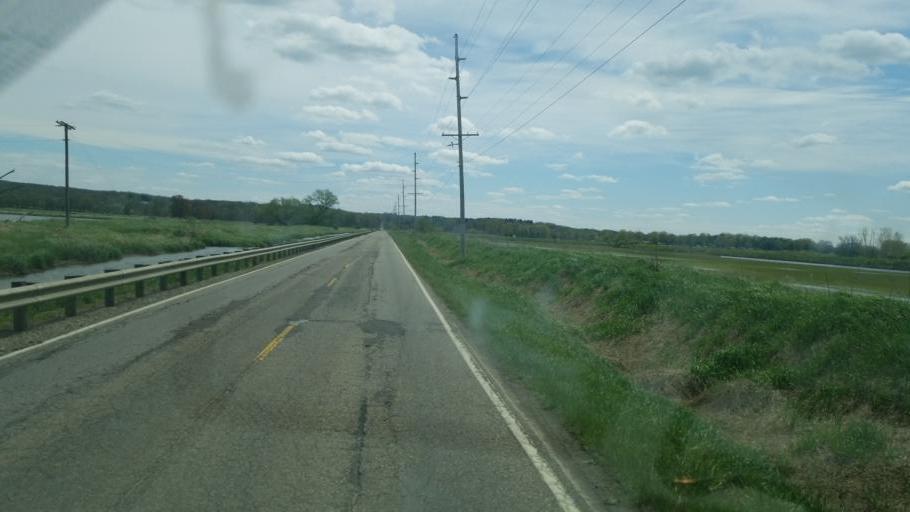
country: US
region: Ohio
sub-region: Wayne County
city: Wooster
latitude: 40.7530
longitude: -81.9443
